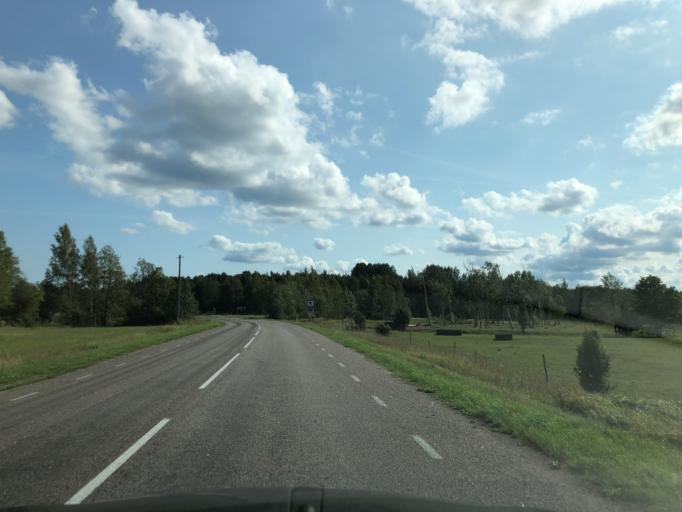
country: EE
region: Hiiumaa
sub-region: Kaerdla linn
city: Kardla
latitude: 58.7209
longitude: 22.5632
